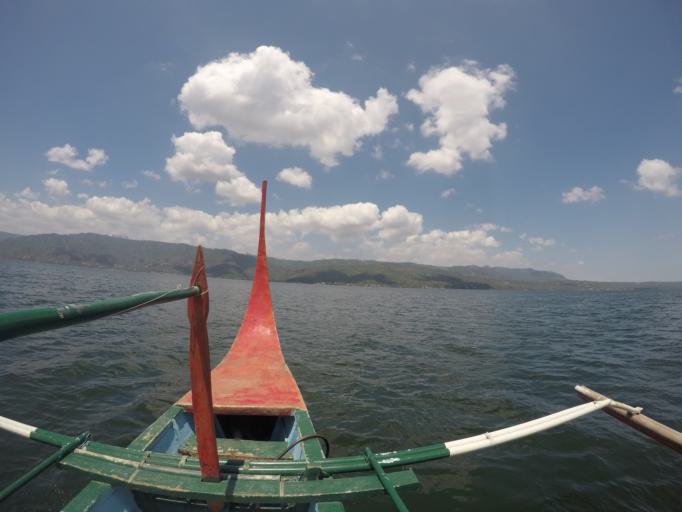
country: PH
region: Calabarzon
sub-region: Province of Batangas
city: Sampaloc
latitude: 14.0603
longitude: 120.9949
